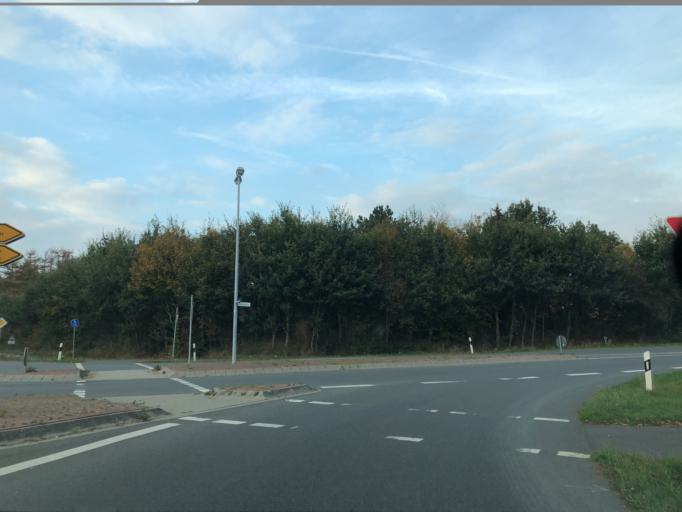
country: DE
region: Lower Saxony
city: Papenburg
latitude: 53.0397
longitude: 7.3917
